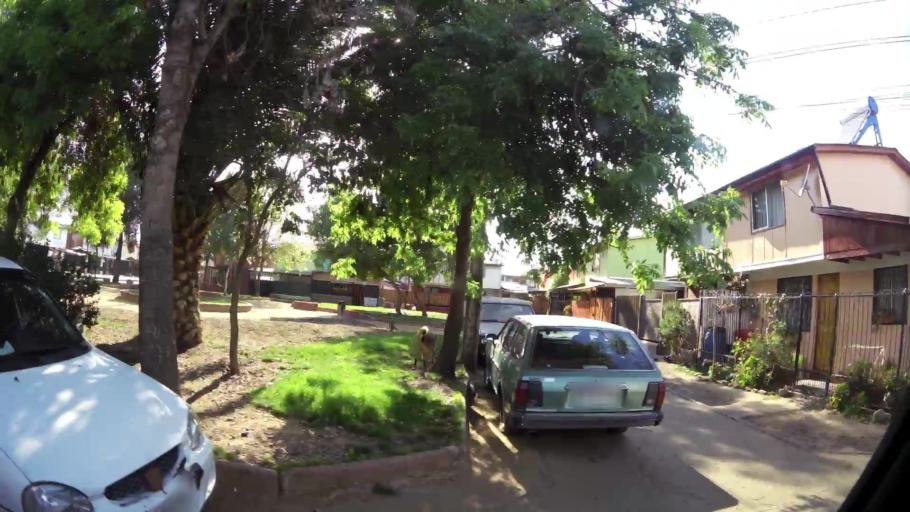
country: CL
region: Santiago Metropolitan
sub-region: Provincia de Talagante
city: Talagante
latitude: -33.6743
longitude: -70.9439
